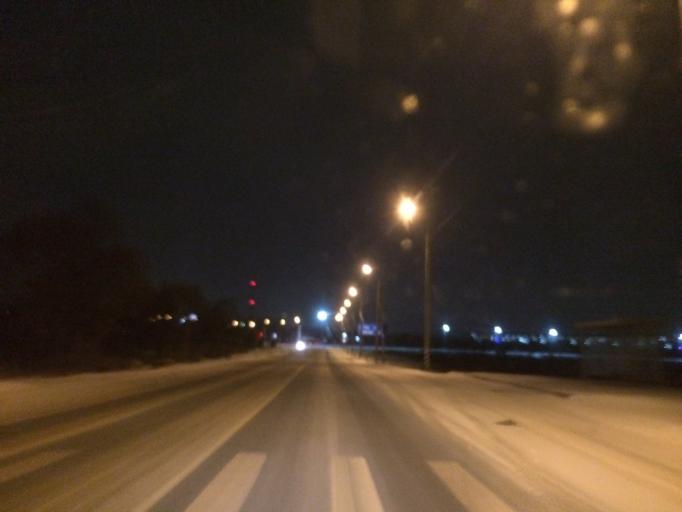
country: RU
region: Tula
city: Gorelki
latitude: 54.2382
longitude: 37.6588
